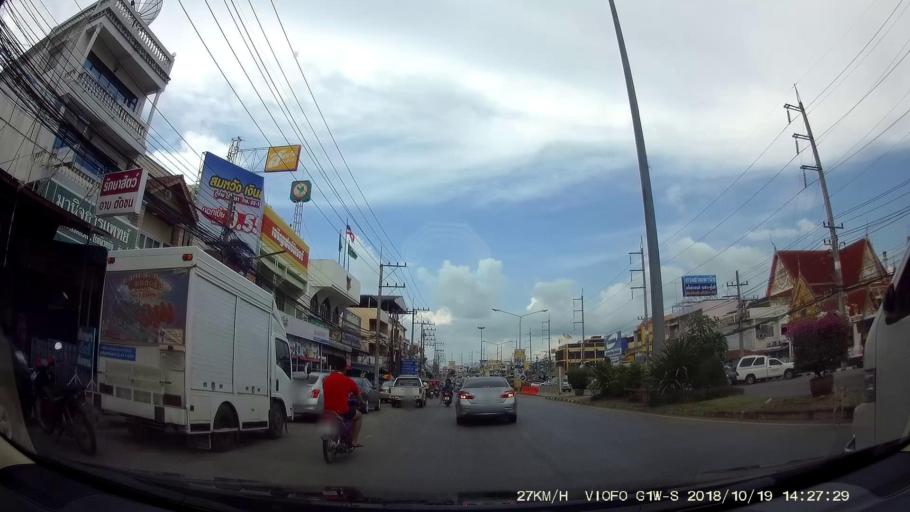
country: TH
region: Chaiyaphum
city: Kaeng Khro
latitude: 16.1116
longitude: 102.2579
